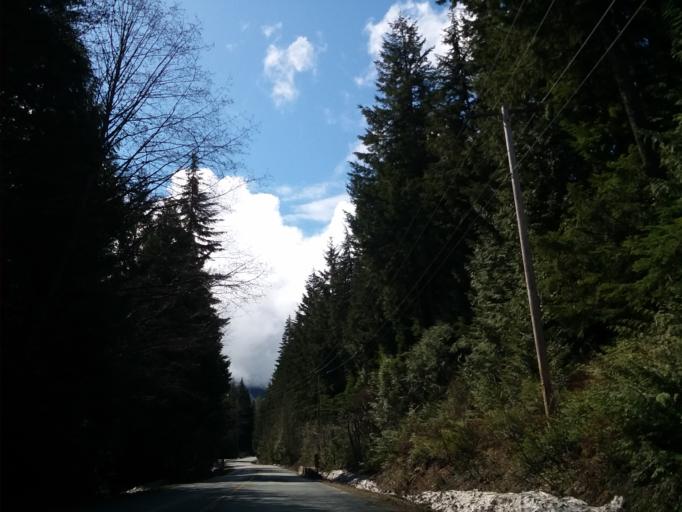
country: CA
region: British Columbia
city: Whistler
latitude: 50.1089
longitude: -122.9895
